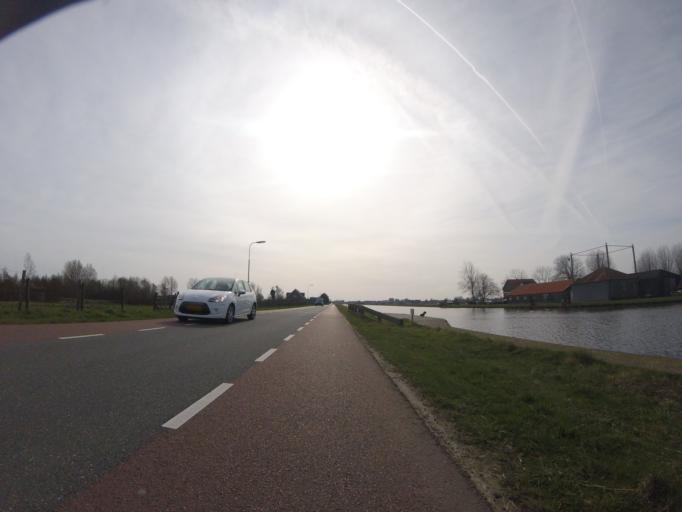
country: NL
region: North Holland
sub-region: Gemeente Bloemendaal
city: Bennebroek
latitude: 52.3048
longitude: 4.6041
